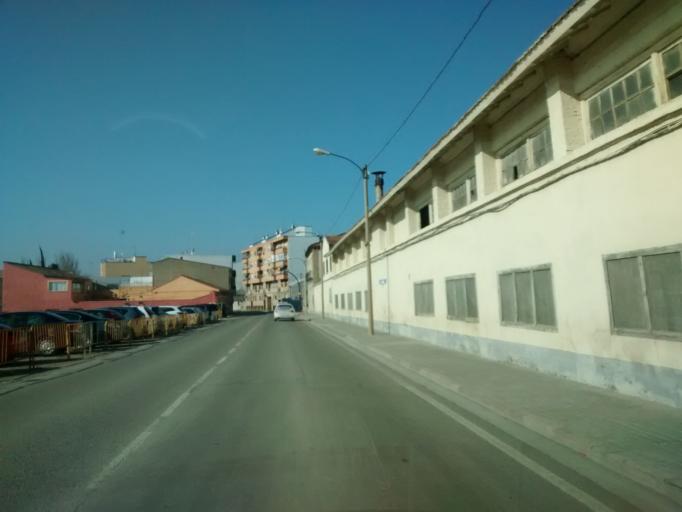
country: ES
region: Aragon
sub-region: Provincia de Zaragoza
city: Zaragoza
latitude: 41.6922
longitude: -0.8236
